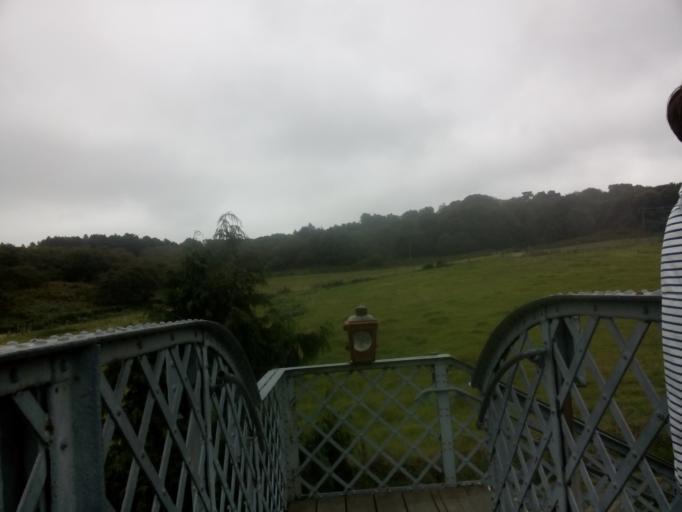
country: GB
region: England
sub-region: Norfolk
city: Sheringham
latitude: 52.9329
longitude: 1.1505
